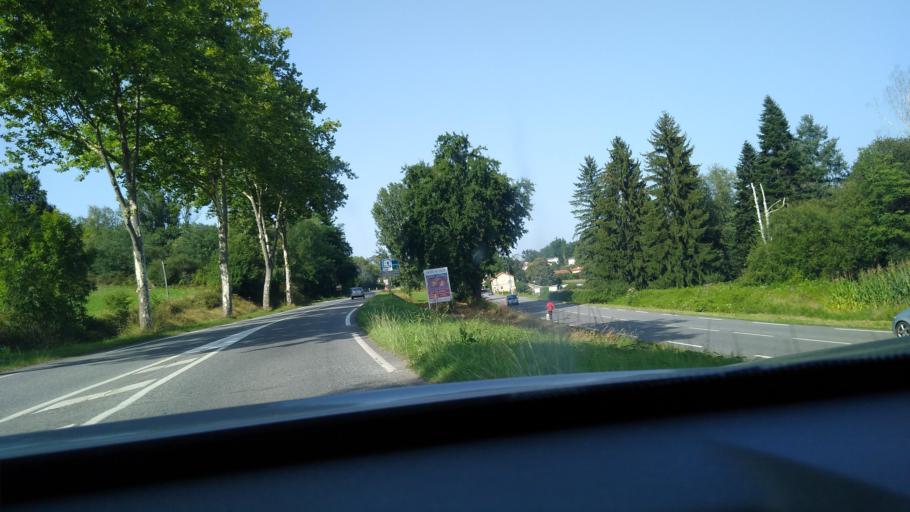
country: FR
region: Midi-Pyrenees
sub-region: Departement de la Haute-Garonne
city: Salies-du-Salat
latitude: 43.0929
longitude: 0.9504
